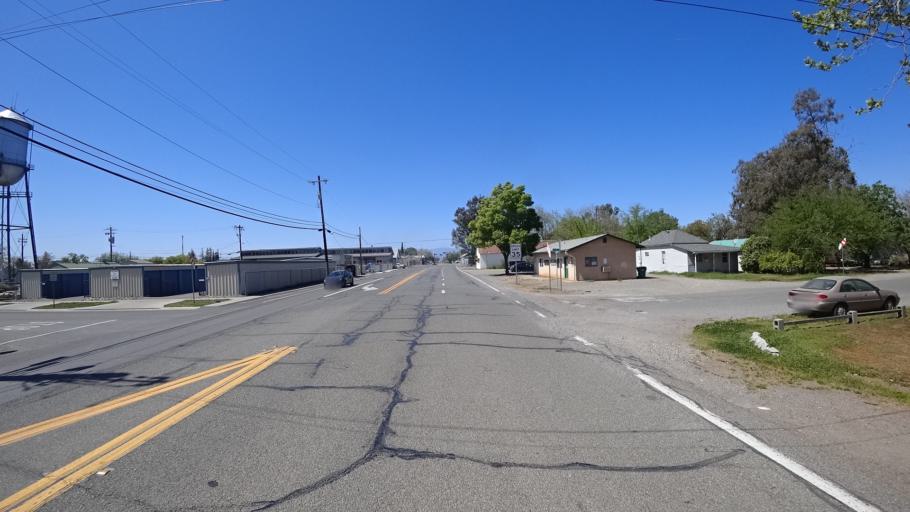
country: US
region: California
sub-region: Glenn County
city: Willows
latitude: 39.5243
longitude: -122.1907
